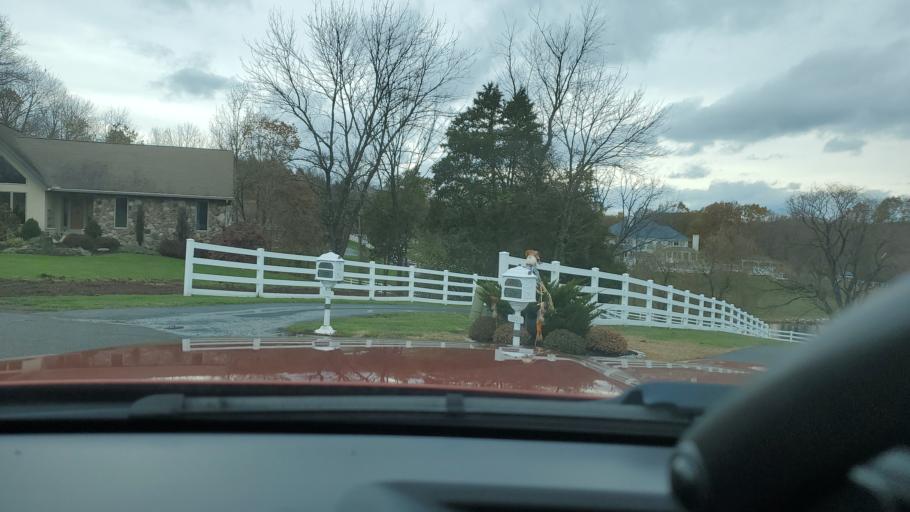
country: US
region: Pennsylvania
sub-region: Montgomery County
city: Spring Mount
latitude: 40.2936
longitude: -75.5089
